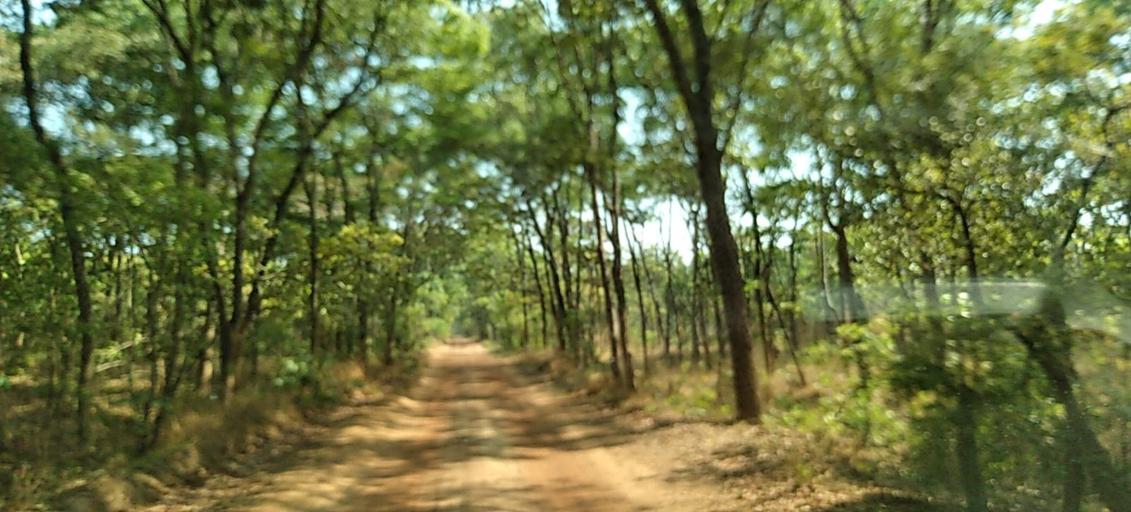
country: ZM
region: Copperbelt
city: Kalulushi
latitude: -12.9295
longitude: 27.8217
